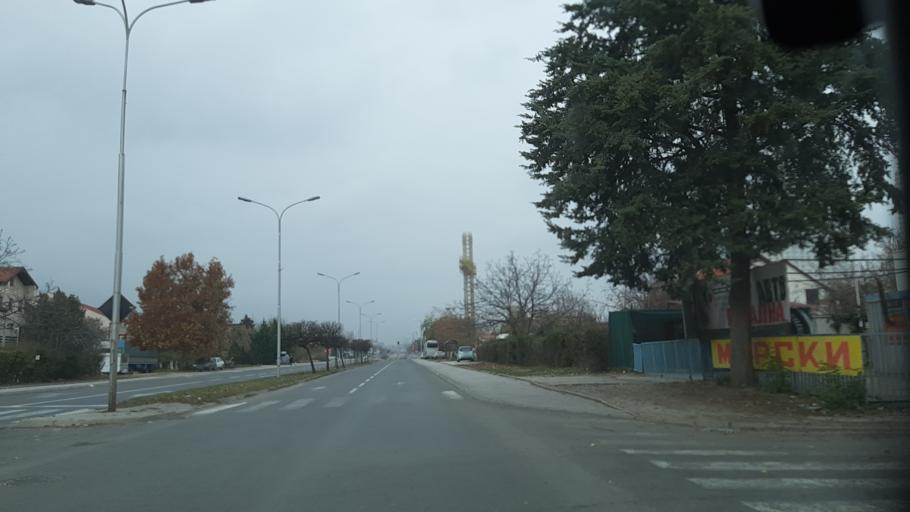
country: MK
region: Kisela Voda
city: Usje
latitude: 41.9758
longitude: 21.4678
